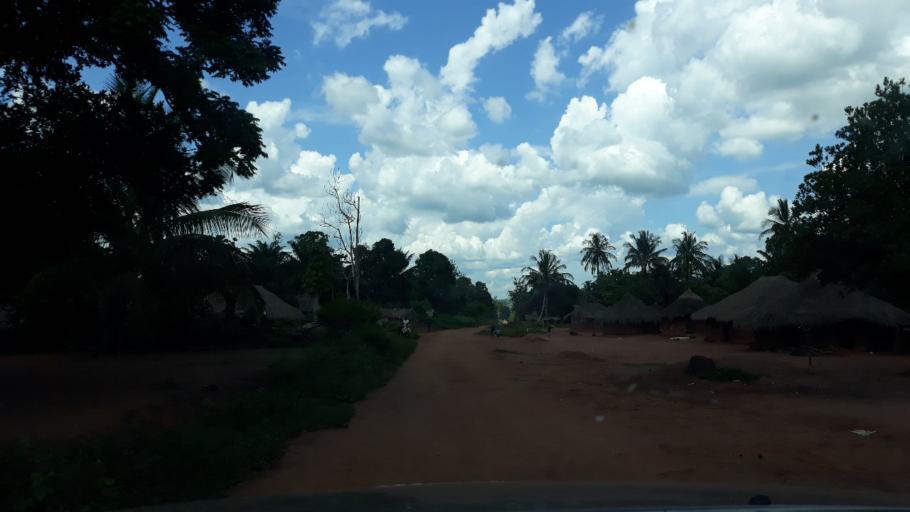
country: CD
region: Equateur
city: Businga
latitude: 3.4094
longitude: 20.4014
